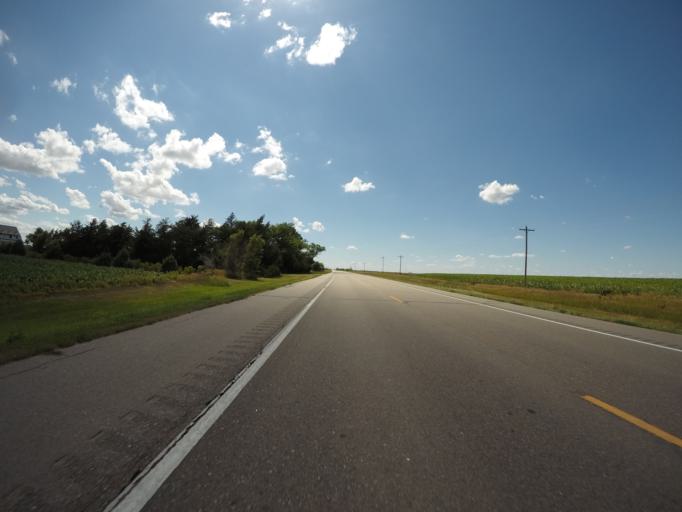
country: US
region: Nebraska
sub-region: Chase County
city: Imperial
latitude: 40.4952
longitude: -101.5468
